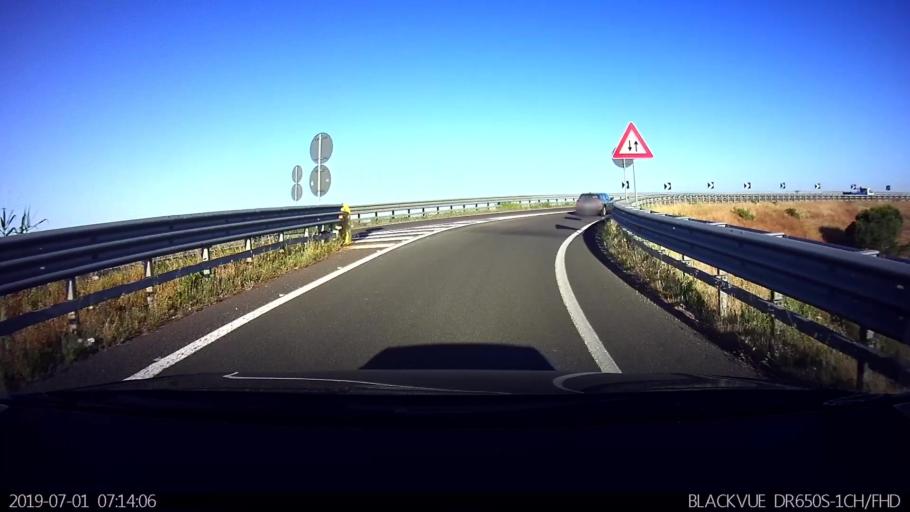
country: IT
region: Latium
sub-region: Provincia di Latina
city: Borgo Hermada
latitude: 41.3204
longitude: 13.1839
